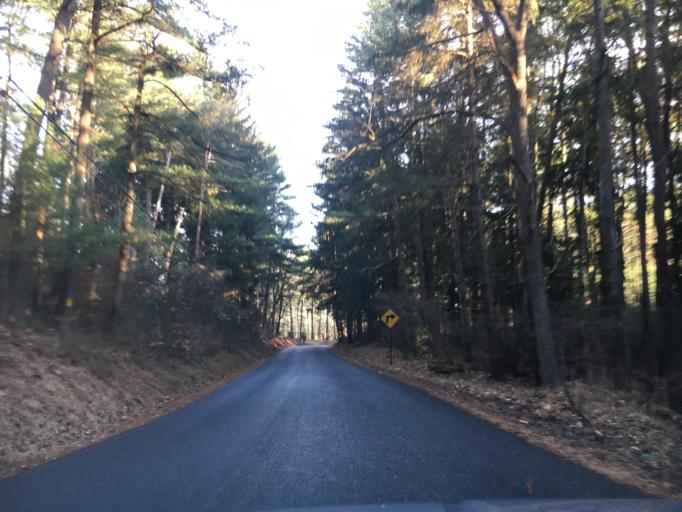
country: US
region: Pennsylvania
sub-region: Carbon County
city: Lehighton
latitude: 40.7903
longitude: -75.7176
